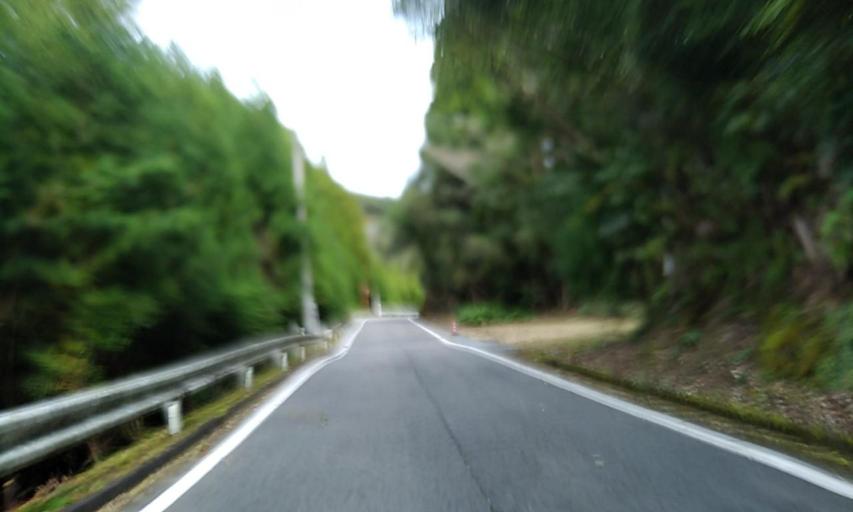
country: JP
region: Wakayama
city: Shingu
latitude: 33.5421
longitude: 135.8384
